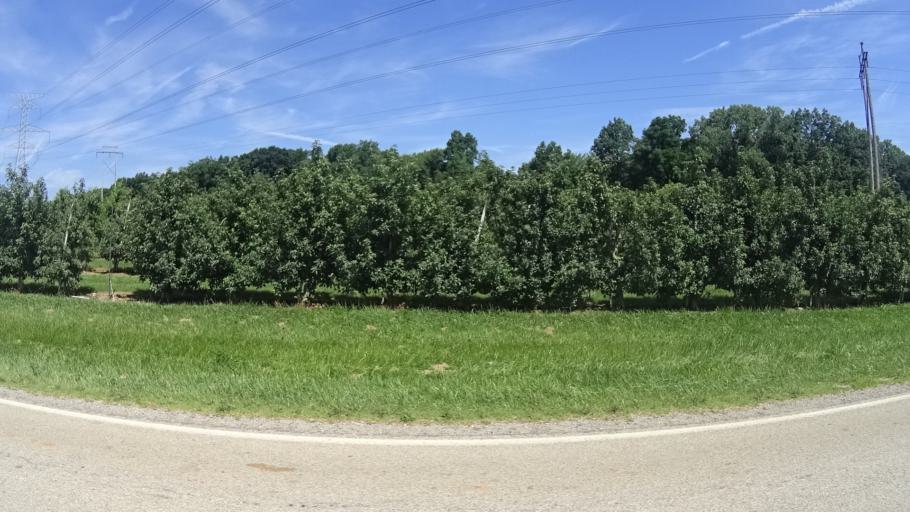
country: US
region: Ohio
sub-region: Erie County
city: Huron
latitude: 41.3361
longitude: -82.4776
